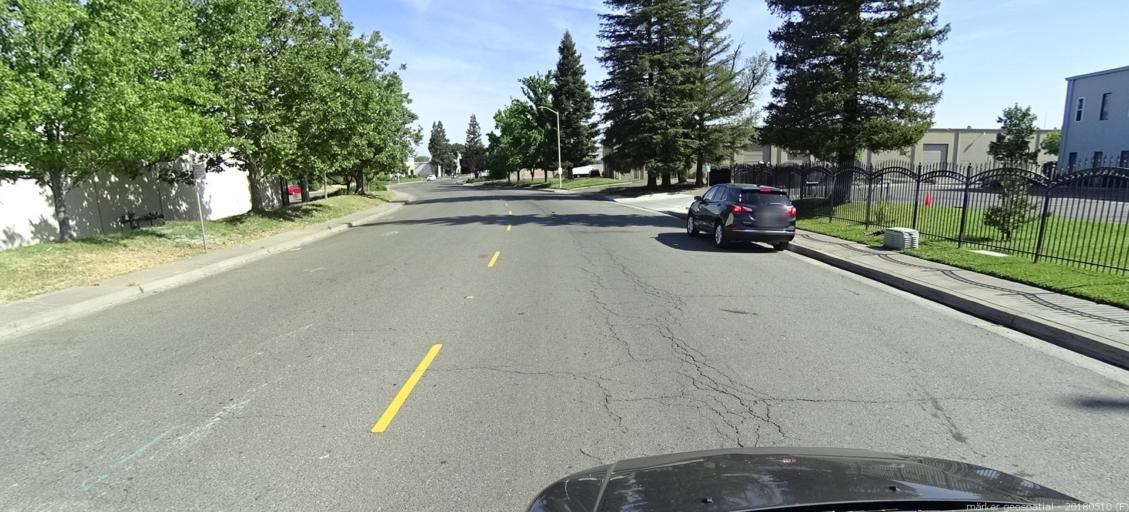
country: US
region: California
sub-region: Sacramento County
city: Rio Linda
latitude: 38.6517
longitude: -121.4716
